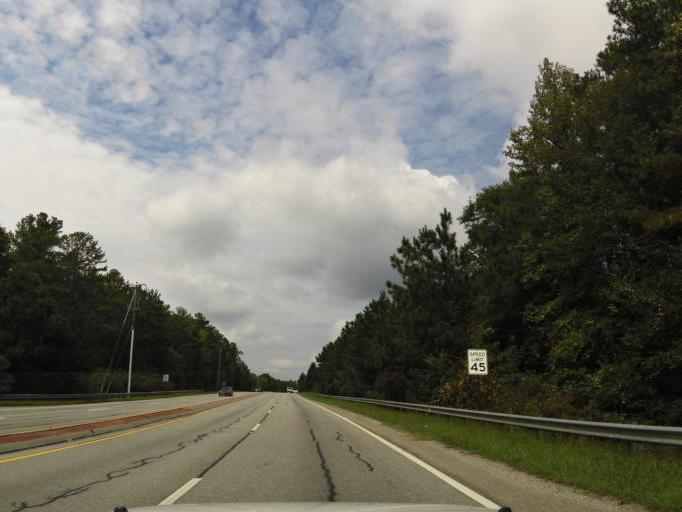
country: US
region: Georgia
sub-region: Cobb County
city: Powder Springs
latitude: 33.9201
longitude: -84.6288
